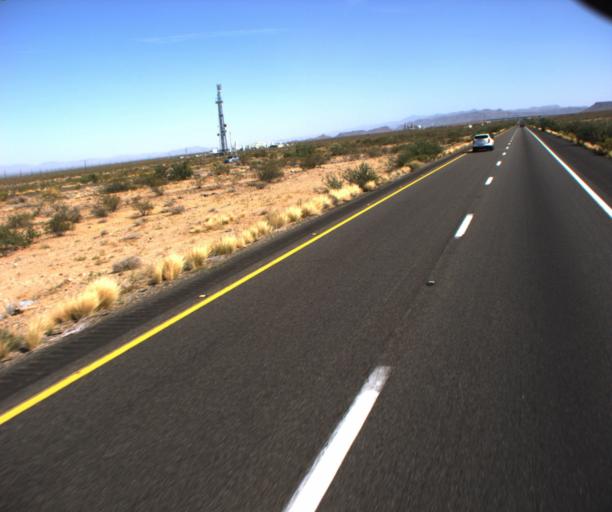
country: US
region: Arizona
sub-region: Mohave County
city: Kingman
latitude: 35.0191
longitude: -114.1328
